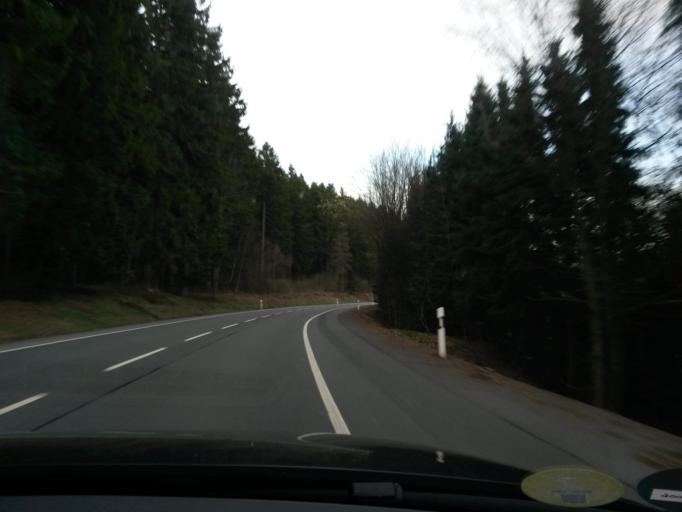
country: DE
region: North Rhine-Westphalia
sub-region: Regierungsbezirk Arnsberg
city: Herscheid
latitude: 51.1241
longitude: 7.7488
